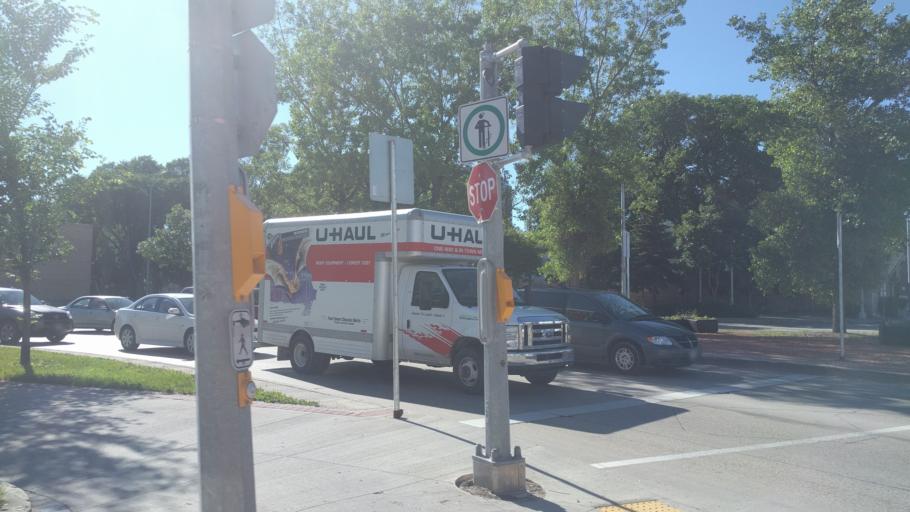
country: CA
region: Manitoba
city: Winnipeg
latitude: 49.8835
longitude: -97.1319
